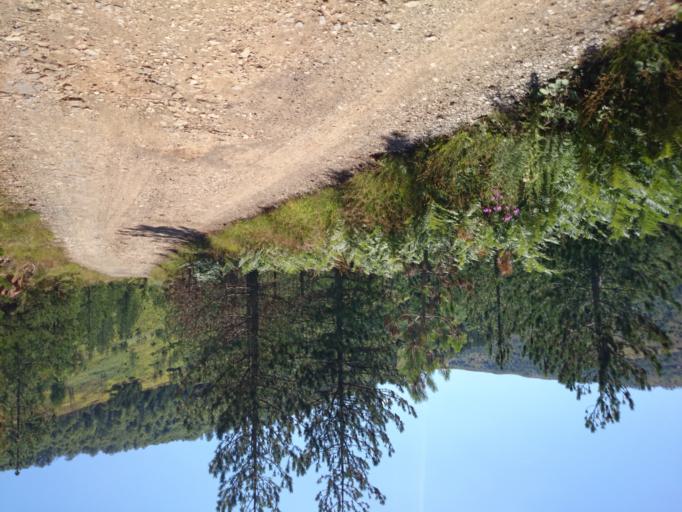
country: AL
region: Diber
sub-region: Rrethi i Bulqizes
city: Zerqan
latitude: 41.4297
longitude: 20.3261
